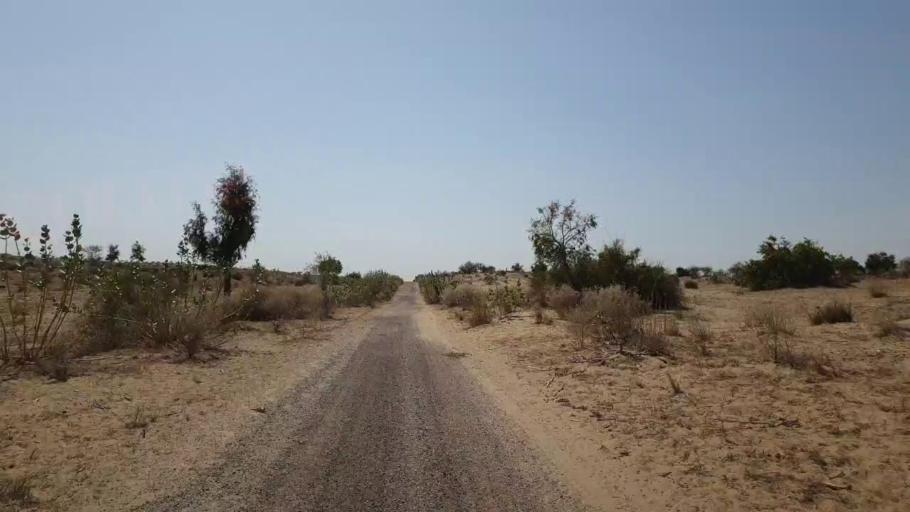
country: PK
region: Sindh
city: Umarkot
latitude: 25.1797
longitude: 69.8770
